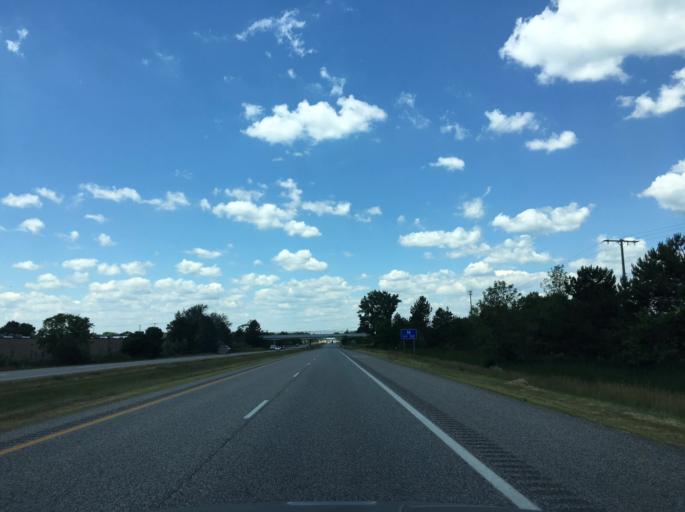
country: US
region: Michigan
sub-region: Midland County
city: Midland
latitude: 43.6560
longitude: -84.2231
